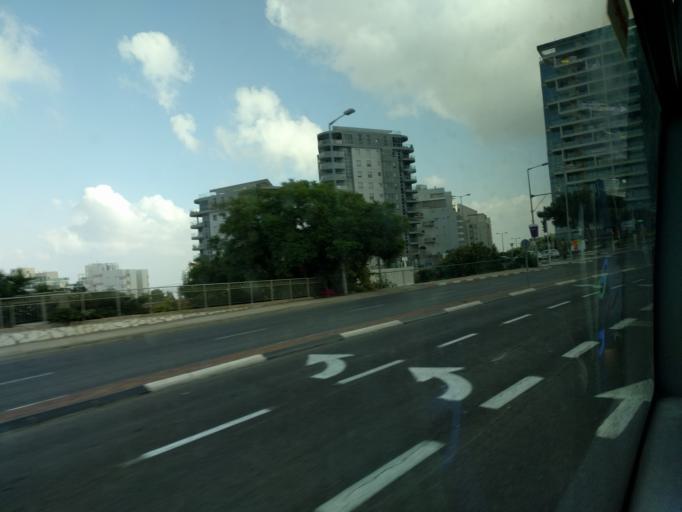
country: IL
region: Haifa
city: Nesher
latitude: 32.7674
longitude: 35.0109
